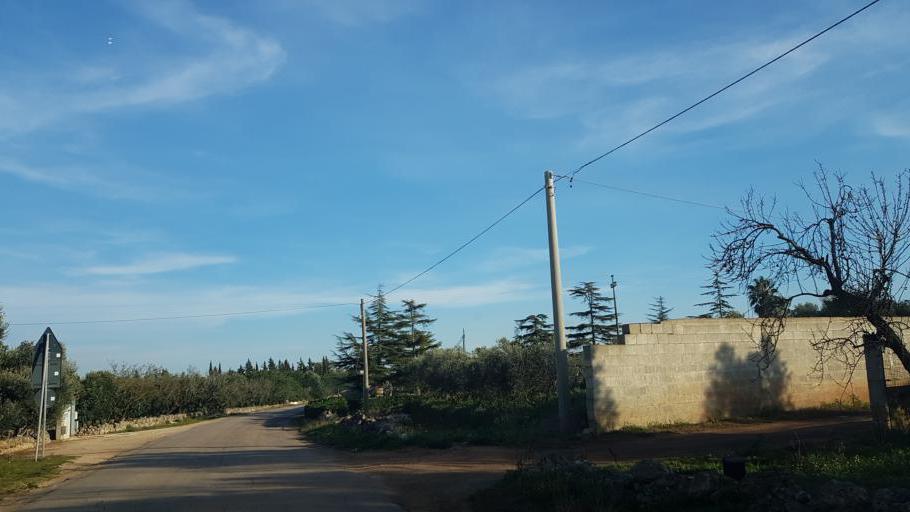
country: IT
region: Apulia
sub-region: Provincia di Brindisi
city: San Vito dei Normanni
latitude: 40.6998
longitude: 17.7351
